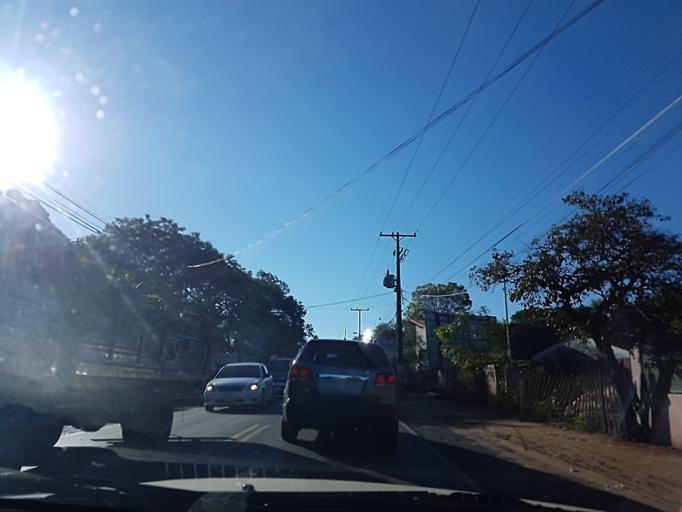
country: PY
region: Central
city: San Lorenzo
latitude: -25.2770
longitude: -57.4771
